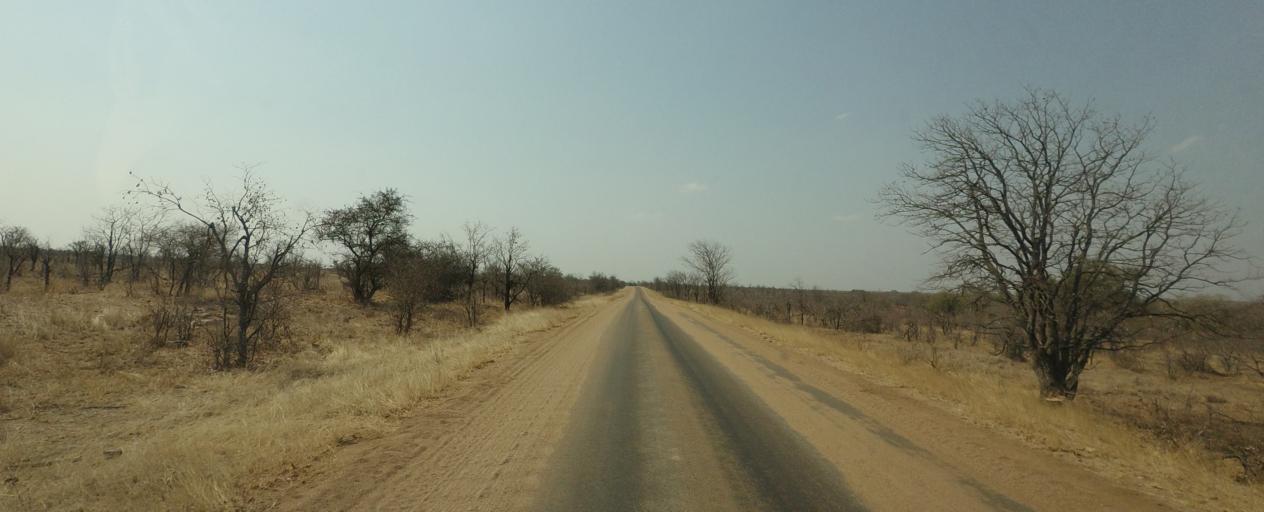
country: ZA
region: Limpopo
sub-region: Mopani District Municipality
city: Giyani
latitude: -23.2205
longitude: 31.3158
